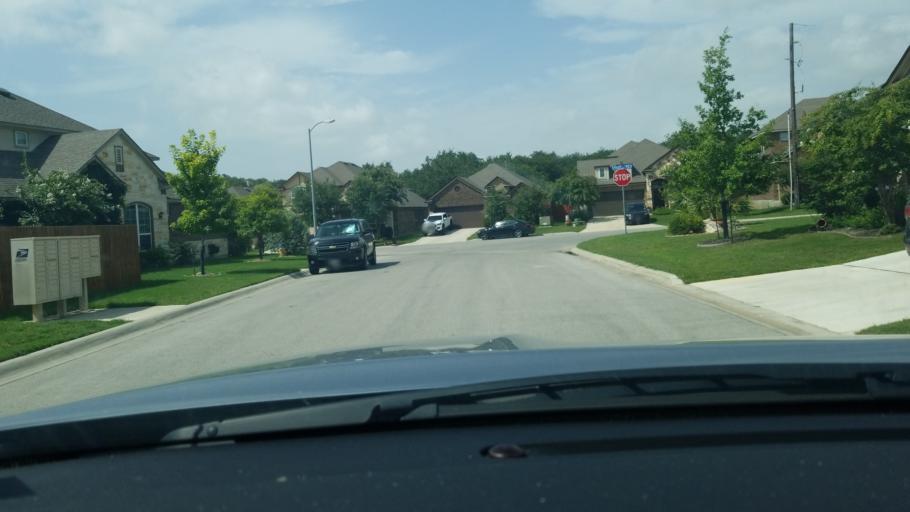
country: US
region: Texas
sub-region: Bexar County
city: Timberwood Park
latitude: 29.6912
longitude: -98.4933
